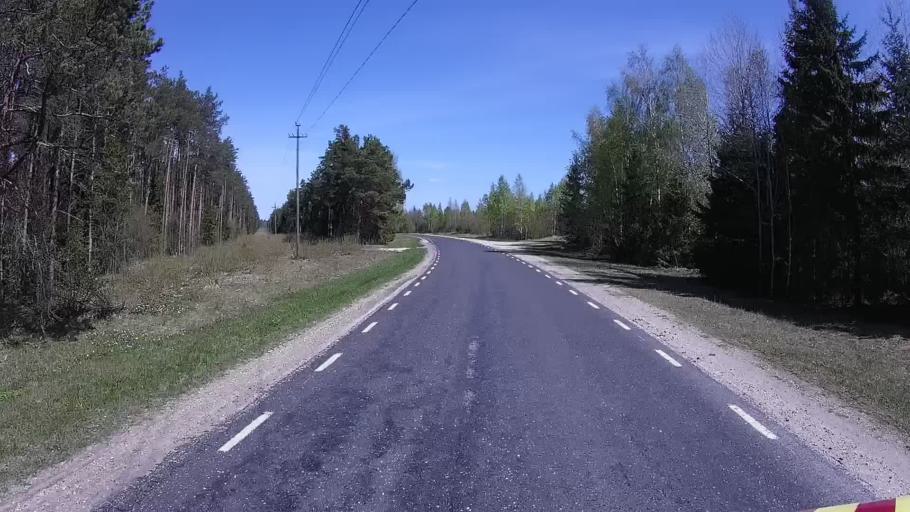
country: EE
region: Laeaene
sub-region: Ridala Parish
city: Uuemoisa
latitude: 59.0354
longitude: 23.8259
